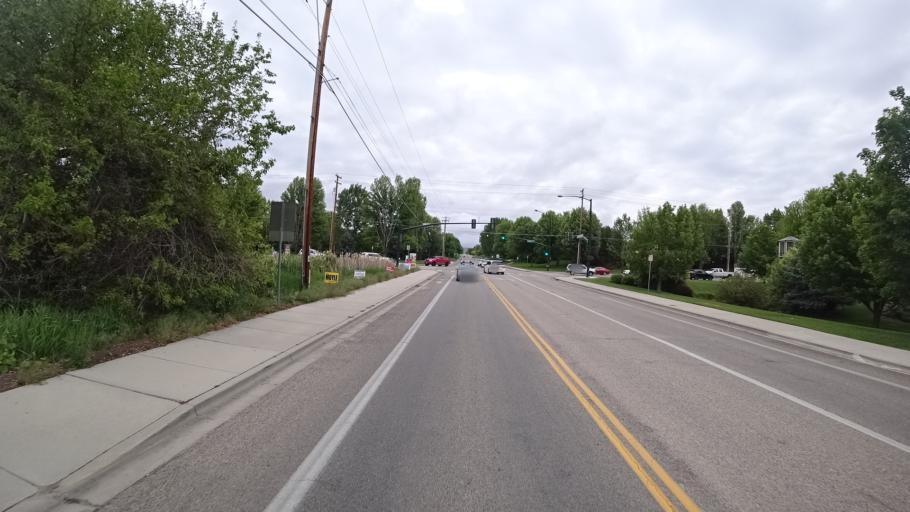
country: US
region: Idaho
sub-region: Ada County
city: Eagle
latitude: 43.7065
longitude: -116.3546
